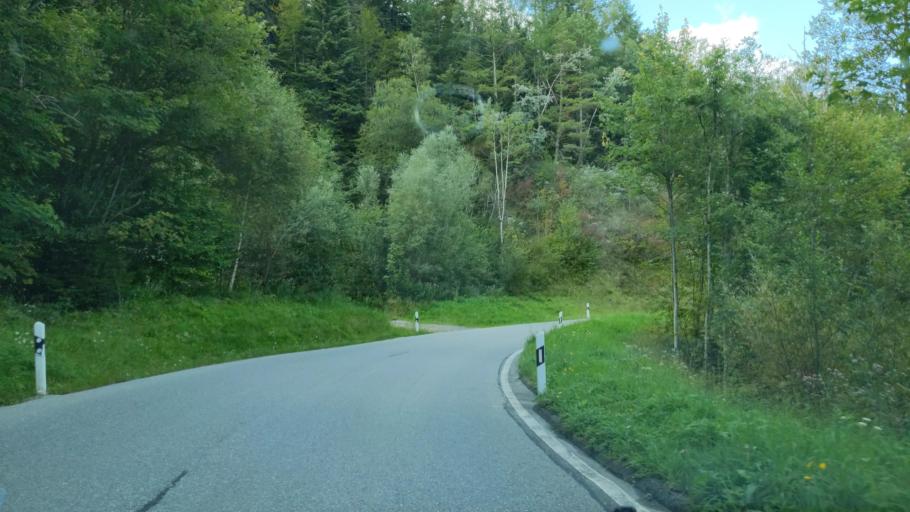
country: CH
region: Saint Gallen
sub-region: Wahlkreis Rheintal
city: Eichberg
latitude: 47.3406
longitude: 9.4935
